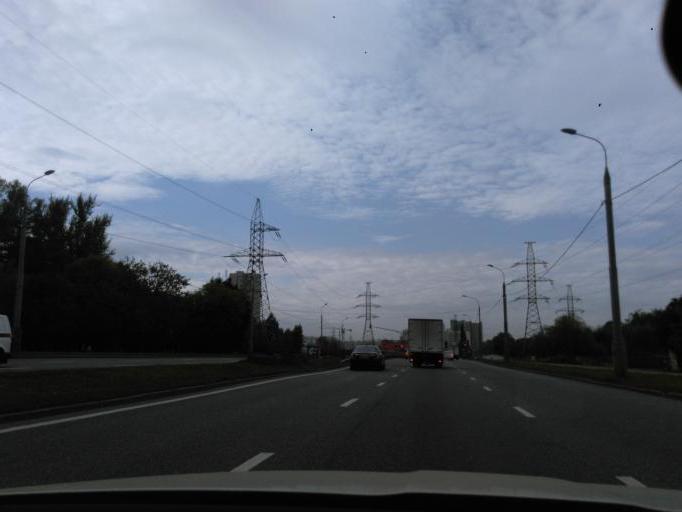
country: RU
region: Moscow
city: Novovladykino
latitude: 55.8418
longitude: 37.5836
